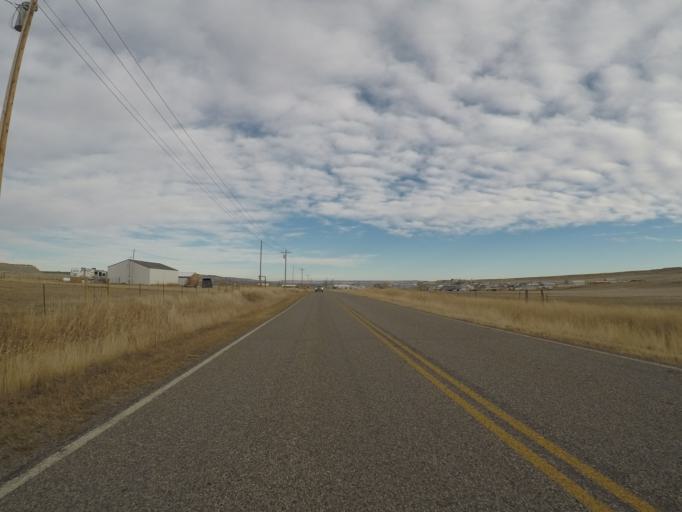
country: US
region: Montana
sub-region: Yellowstone County
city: Laurel
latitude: 45.7840
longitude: -108.7250
